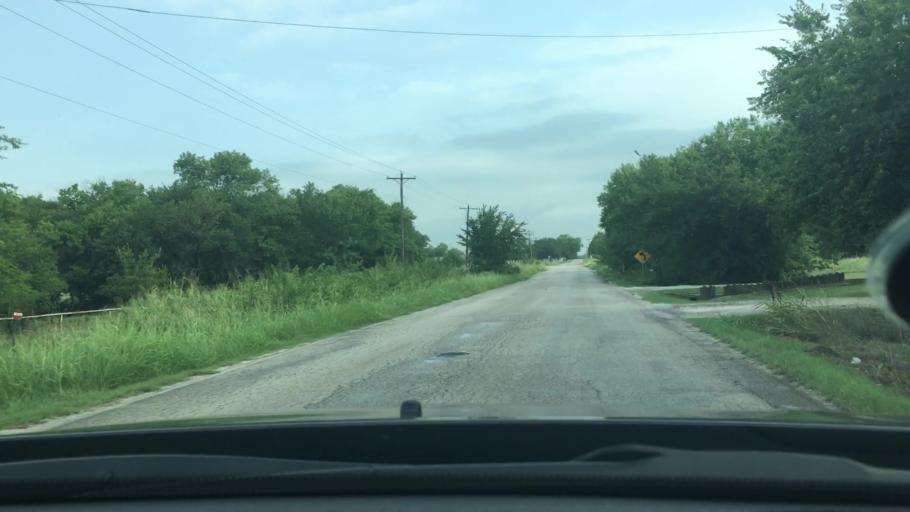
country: US
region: Oklahoma
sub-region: Carter County
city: Lone Grove
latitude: 34.2136
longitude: -97.2650
